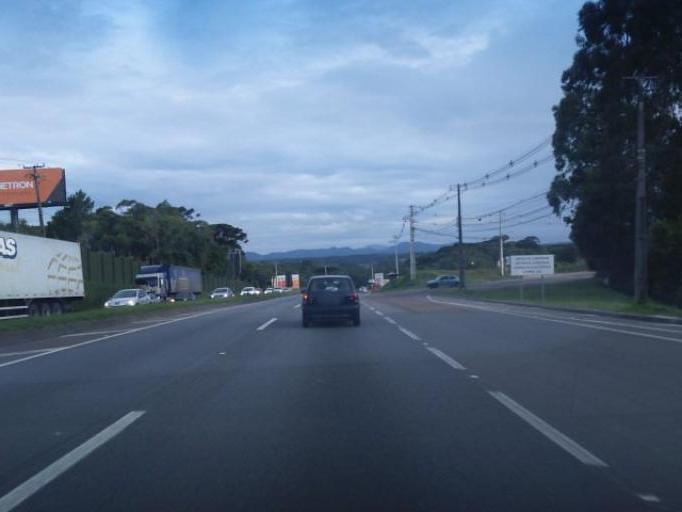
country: BR
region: Parana
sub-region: Sao Jose Dos Pinhais
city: Sao Jose dos Pinhais
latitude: -25.5878
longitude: -49.1725
